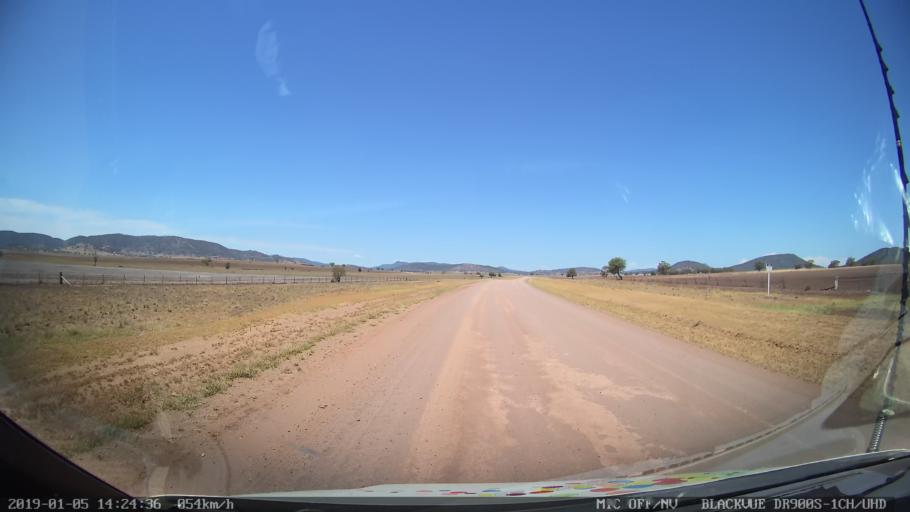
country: AU
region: New South Wales
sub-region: Liverpool Plains
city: Quirindi
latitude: -31.2413
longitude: 150.5416
